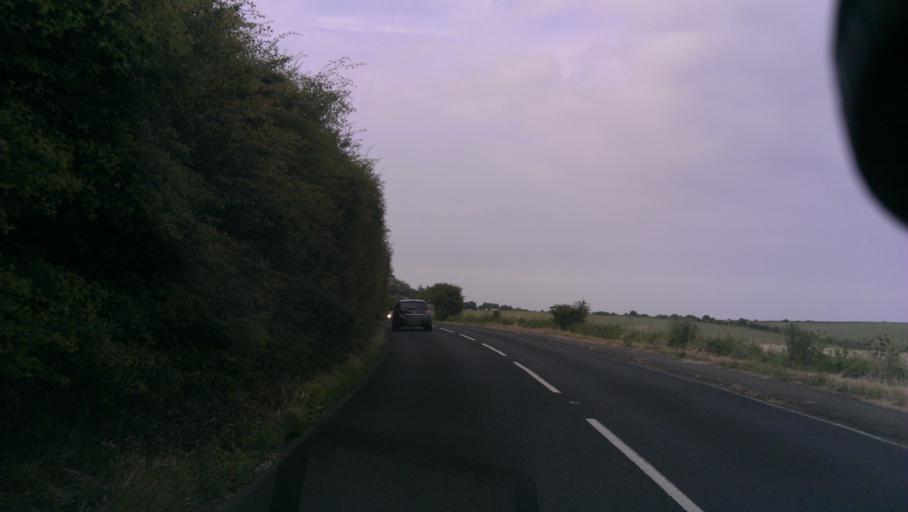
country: GB
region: England
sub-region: Kent
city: Dover
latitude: 51.1355
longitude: 1.3248
